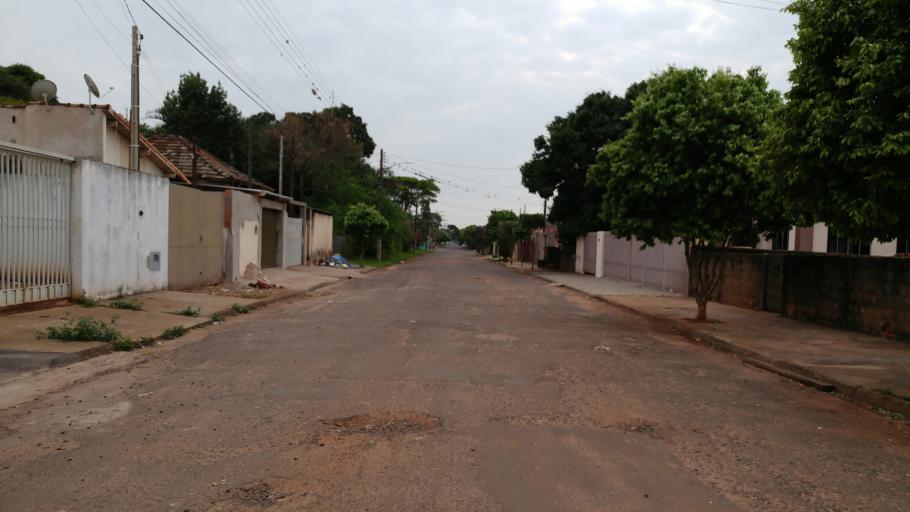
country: BR
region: Sao Paulo
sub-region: Paraguacu Paulista
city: Paraguacu Paulista
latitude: -22.4203
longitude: -50.5717
